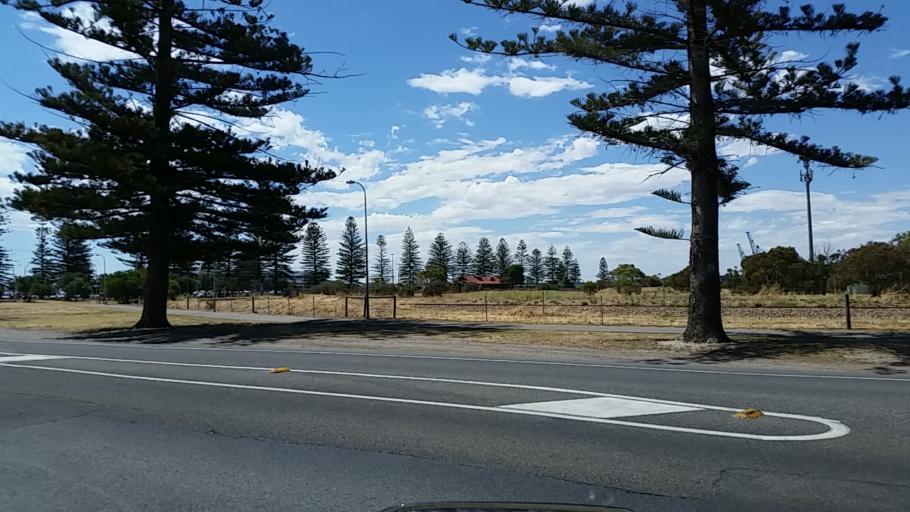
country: AU
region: South Australia
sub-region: Port Adelaide Enfield
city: Birkenhead
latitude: -34.7813
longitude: 138.4842
